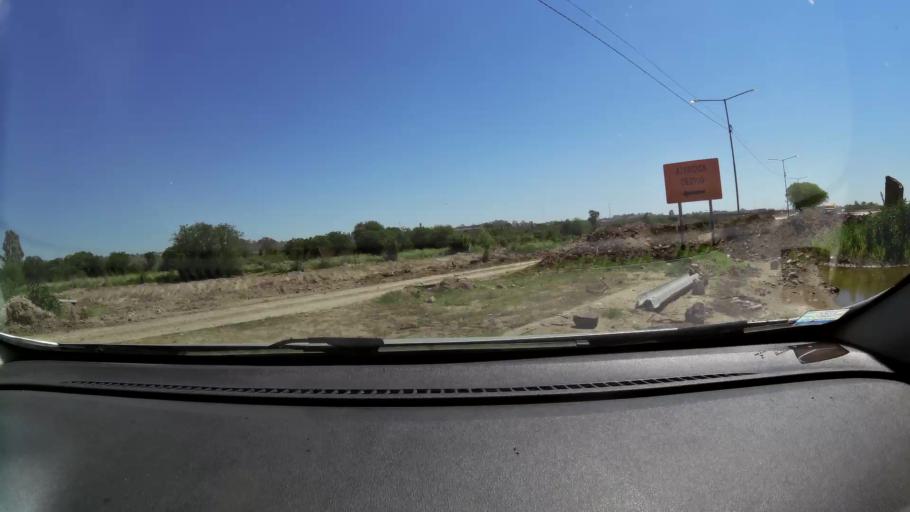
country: AR
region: Cordoba
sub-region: Departamento de Capital
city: Cordoba
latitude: -31.4091
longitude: -64.1278
